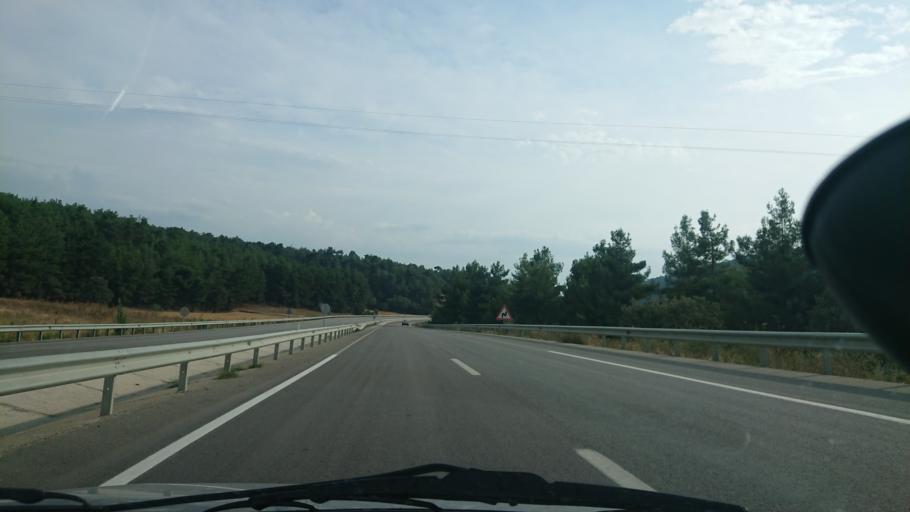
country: TR
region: Kuetahya
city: Gediz
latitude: 38.9191
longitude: 29.3024
